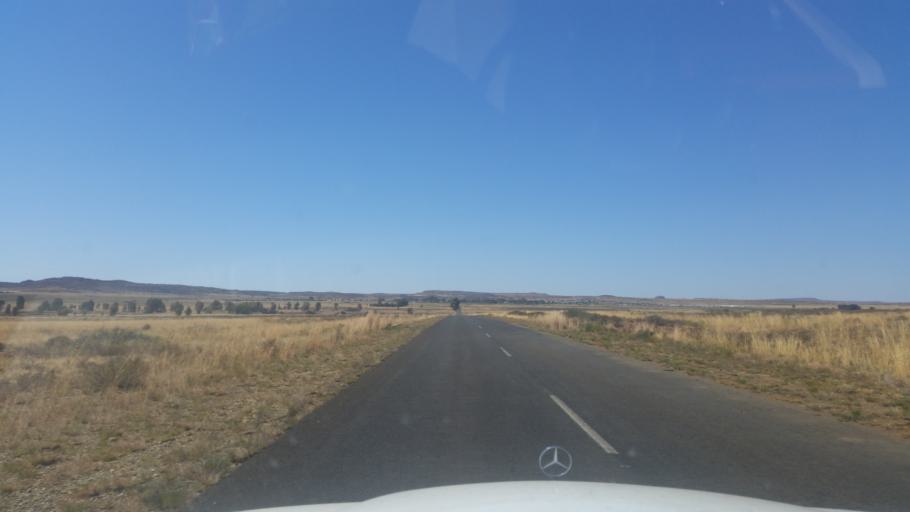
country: ZA
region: Eastern Cape
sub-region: Joe Gqabi District Municipality
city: Burgersdorp
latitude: -30.7516
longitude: 25.7685
